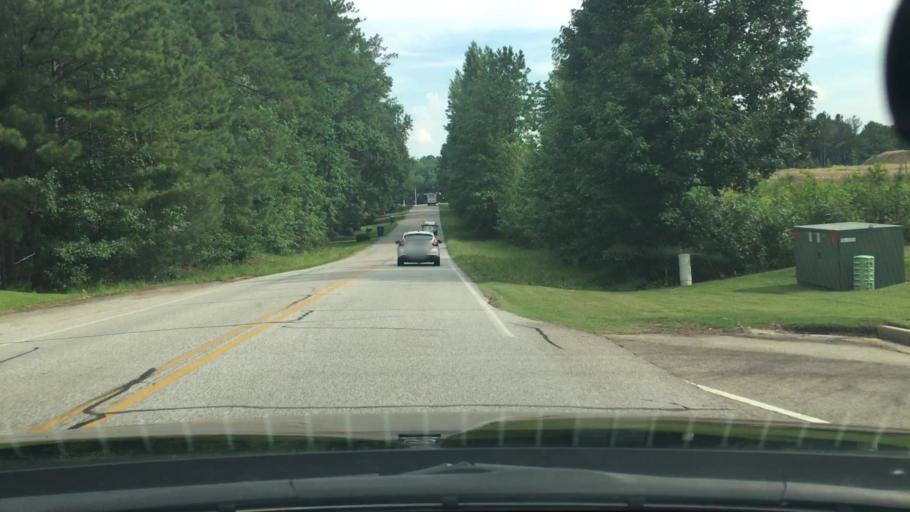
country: US
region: Georgia
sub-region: Coweta County
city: East Newnan
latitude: 33.3777
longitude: -84.7028
